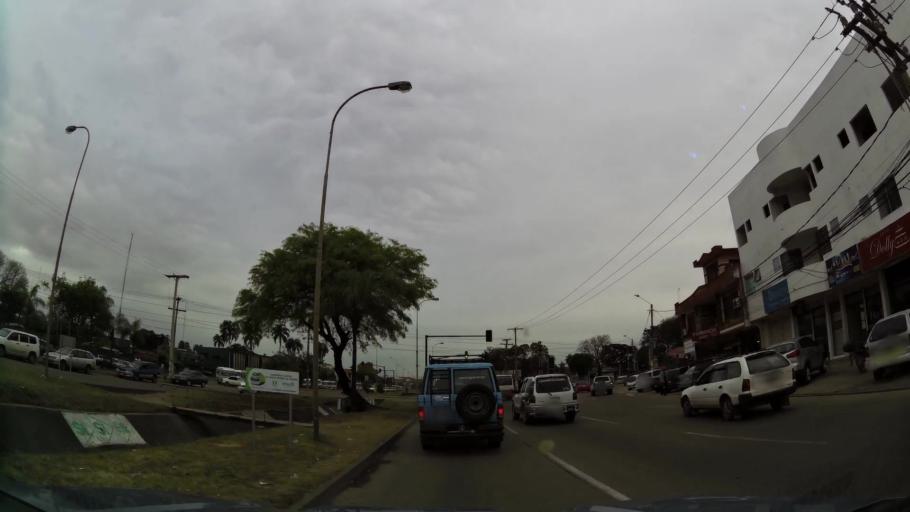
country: BO
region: Santa Cruz
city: Santa Cruz de la Sierra
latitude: -17.8119
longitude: -63.1821
